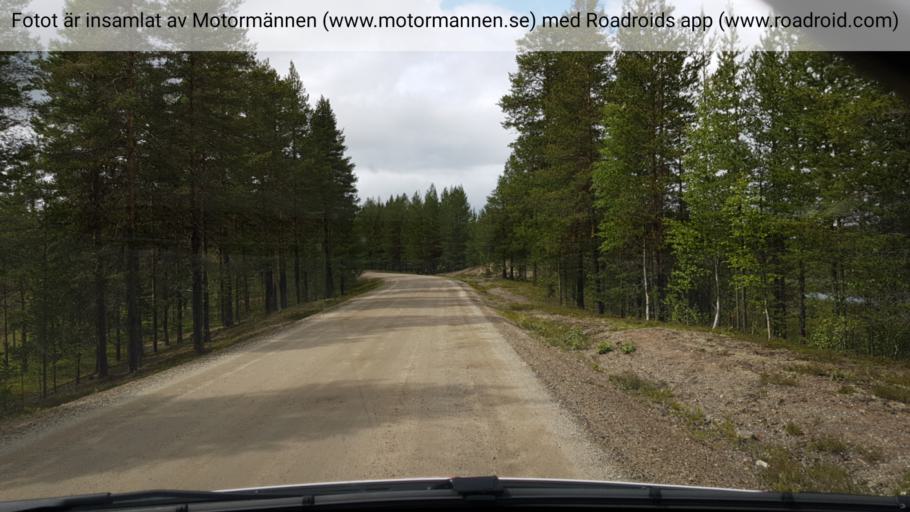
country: SE
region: Vaesterbotten
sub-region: Norsjo Kommun
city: Norsjoe
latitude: 64.5945
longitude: 19.2257
